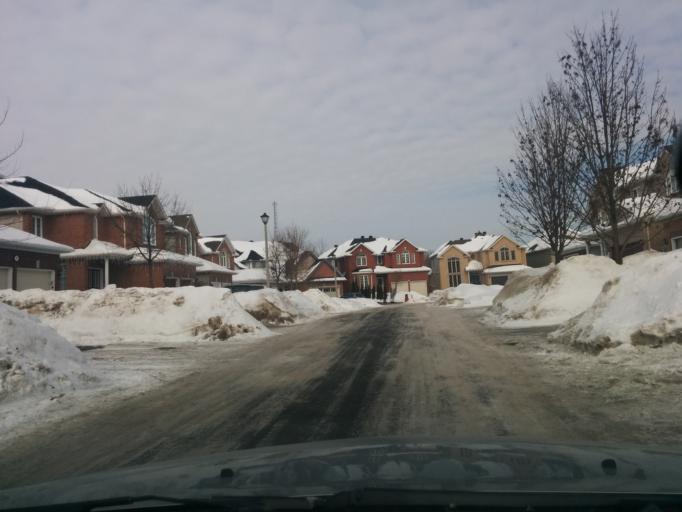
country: CA
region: Ontario
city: Ottawa
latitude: 45.3687
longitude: -75.7400
